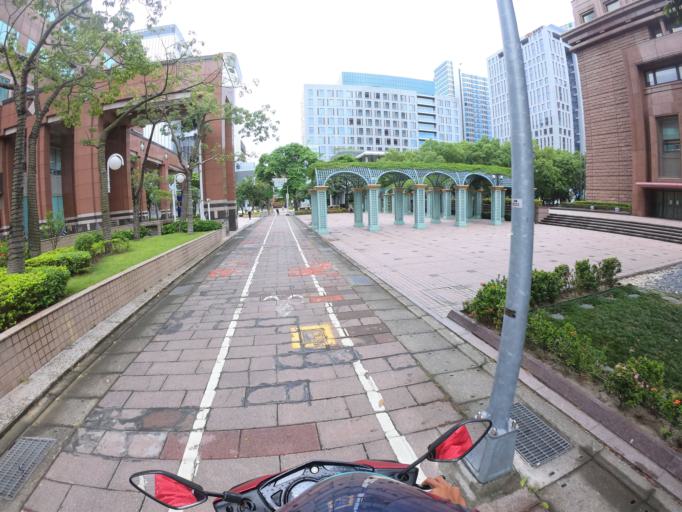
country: TW
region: Taipei
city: Taipei
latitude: 25.0374
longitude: 121.5692
